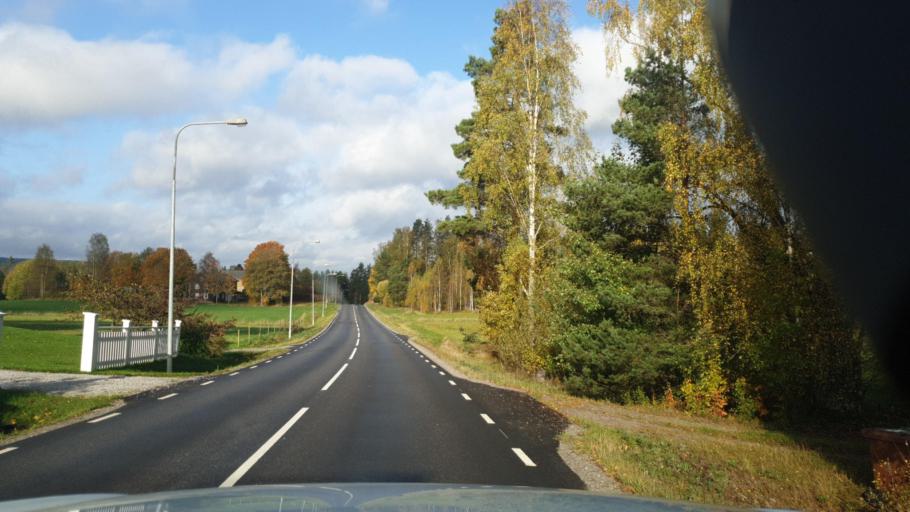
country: SE
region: Vaermland
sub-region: Arvika Kommun
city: Arvika
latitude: 59.5419
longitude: 12.5813
